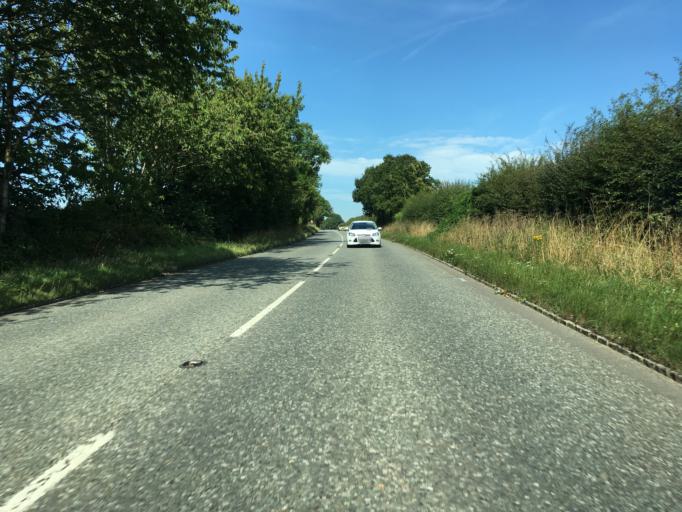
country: GB
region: England
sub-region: West Berkshire
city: Wickham
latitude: 51.4503
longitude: -1.4558
